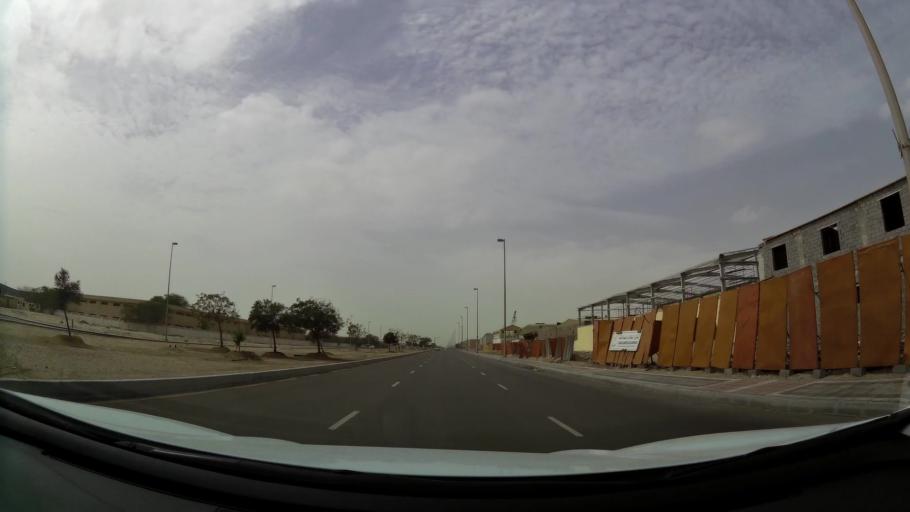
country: AE
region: Abu Dhabi
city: Abu Dhabi
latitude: 24.3684
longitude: 54.4993
